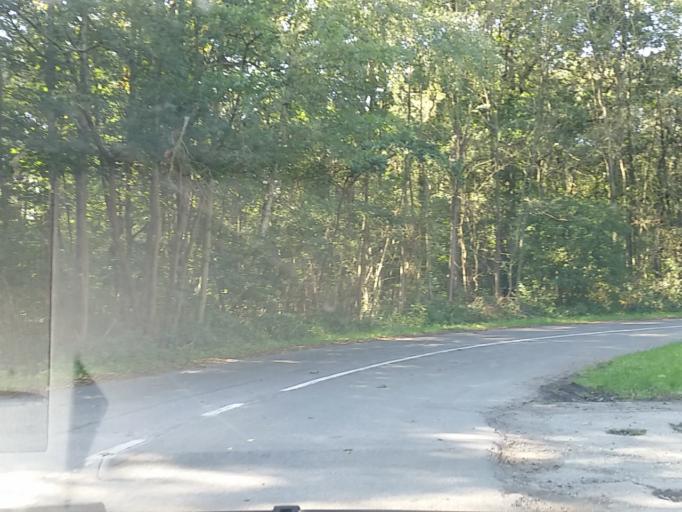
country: BE
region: Flanders
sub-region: Provincie Vlaams-Brabant
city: Machelen
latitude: 50.9214
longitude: 4.4684
